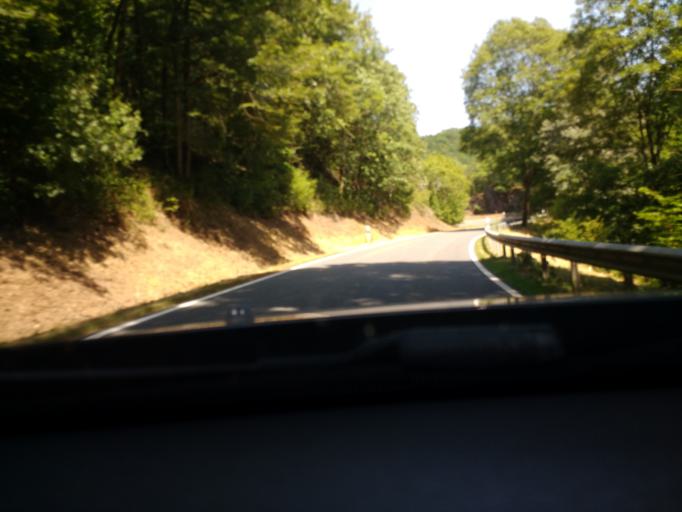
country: DE
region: Rheinland-Pfalz
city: Manderscheid
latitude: 50.0911
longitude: 6.7900
